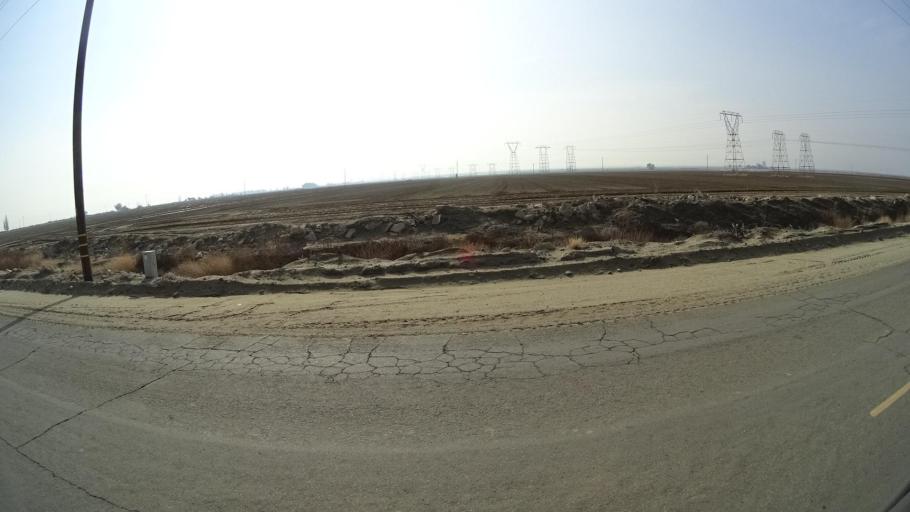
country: US
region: California
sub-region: Kern County
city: Arvin
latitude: 35.0928
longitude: -118.8869
